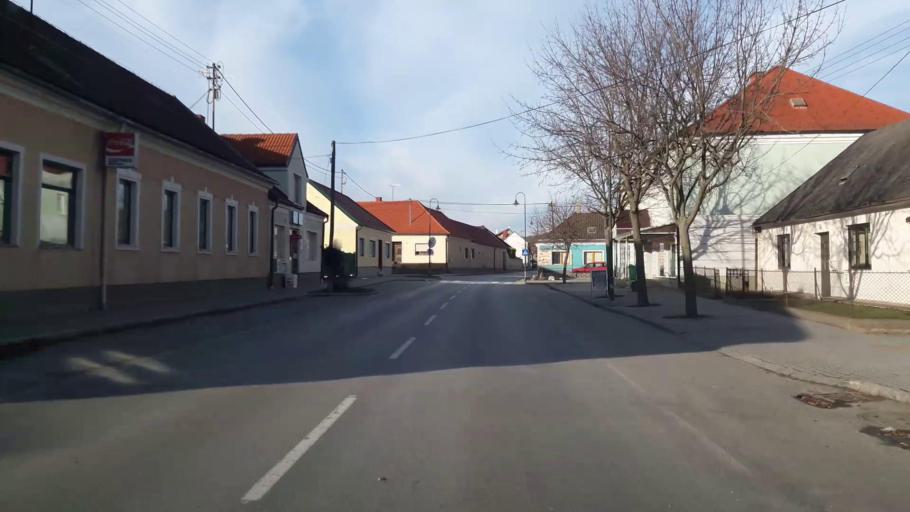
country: AT
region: Lower Austria
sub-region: Politischer Bezirk Ganserndorf
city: Gross-Schweinbarth
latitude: 48.4165
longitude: 16.6331
